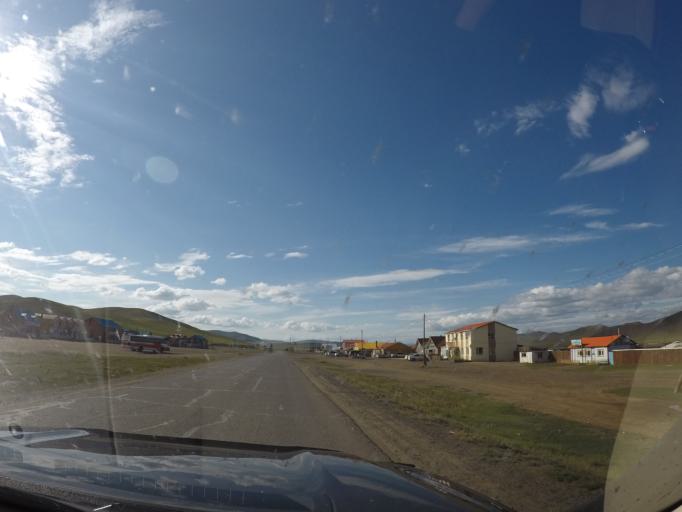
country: MN
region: Hentiy
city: Modot
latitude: 47.7227
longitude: 109.0291
